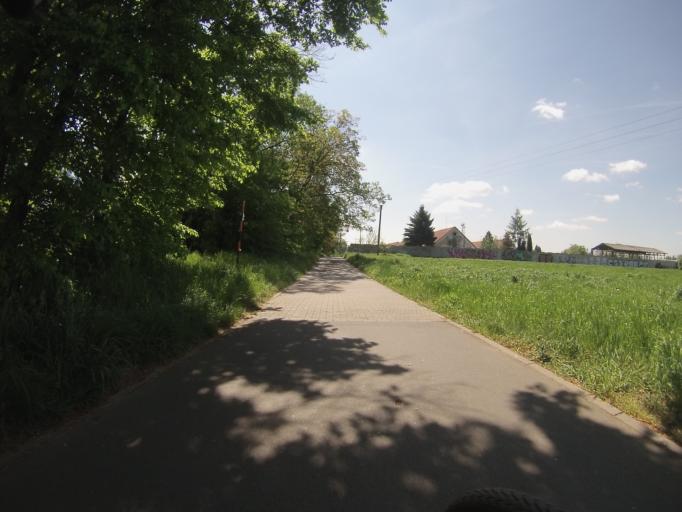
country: CZ
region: South Moravian
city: Modrice
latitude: 49.1535
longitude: 16.6265
